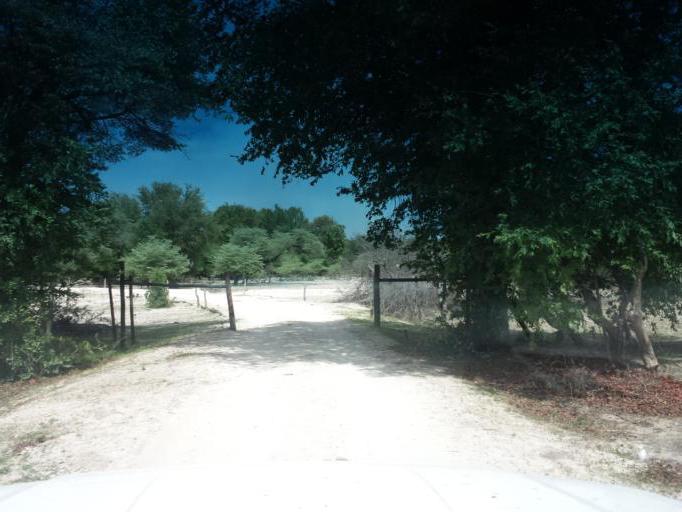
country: BW
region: North West
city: Shakawe
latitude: -18.7484
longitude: 22.1920
